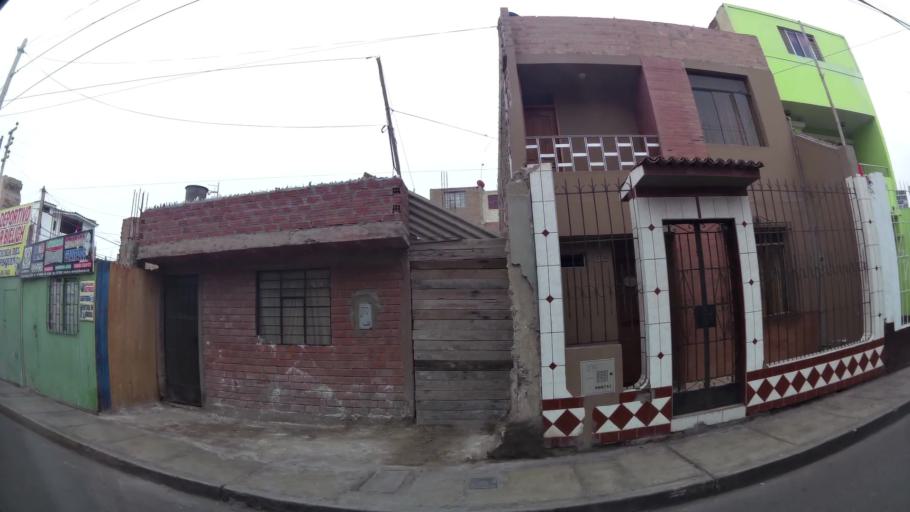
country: PE
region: Ica
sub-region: Provincia de Pisco
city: Pisco
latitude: -13.7114
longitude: -76.2054
